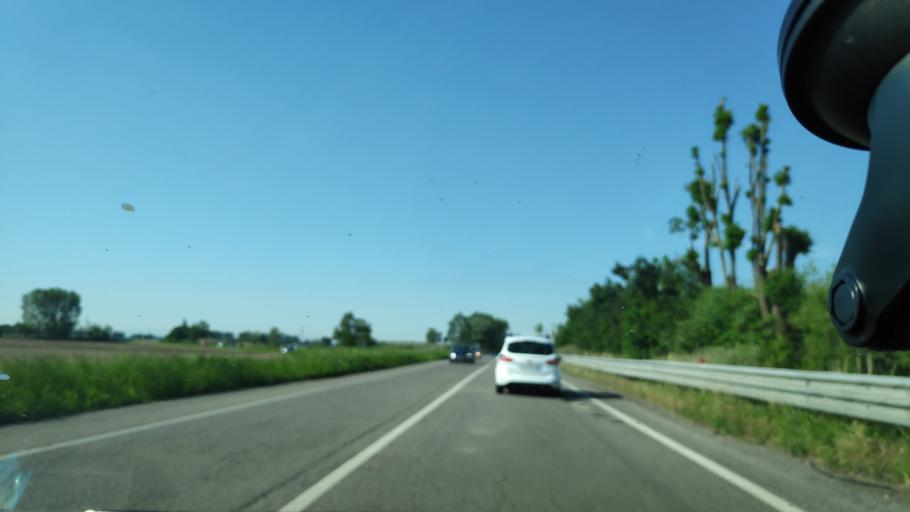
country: IT
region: Lombardy
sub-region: Citta metropolitana di Milano
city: Locate di Triulzi
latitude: 45.3663
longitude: 9.2486
